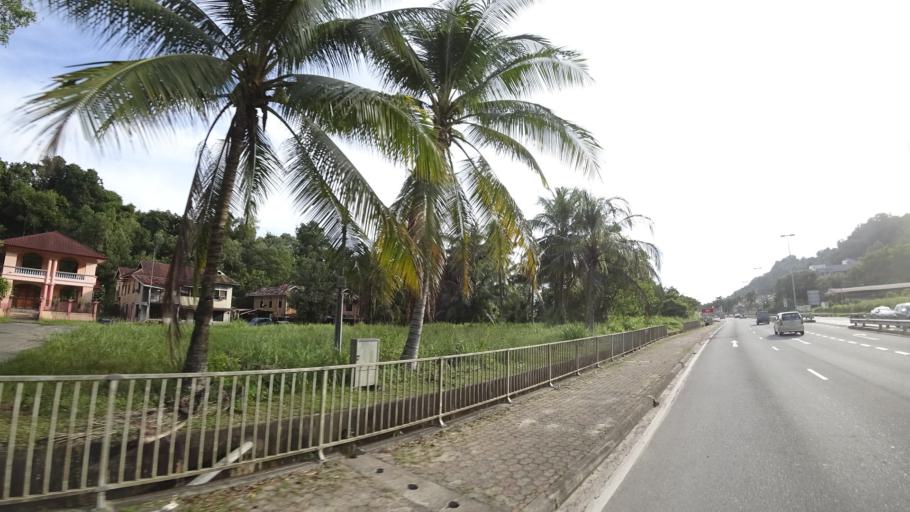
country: BN
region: Brunei and Muara
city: Bandar Seri Begawan
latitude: 4.8626
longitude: 114.9002
